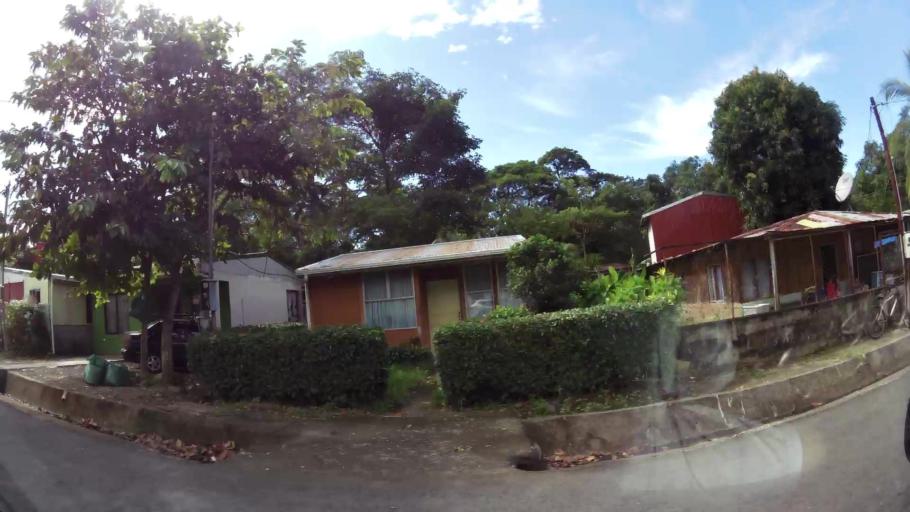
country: CR
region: Guanacaste
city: Juntas
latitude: 10.2808
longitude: -84.9473
